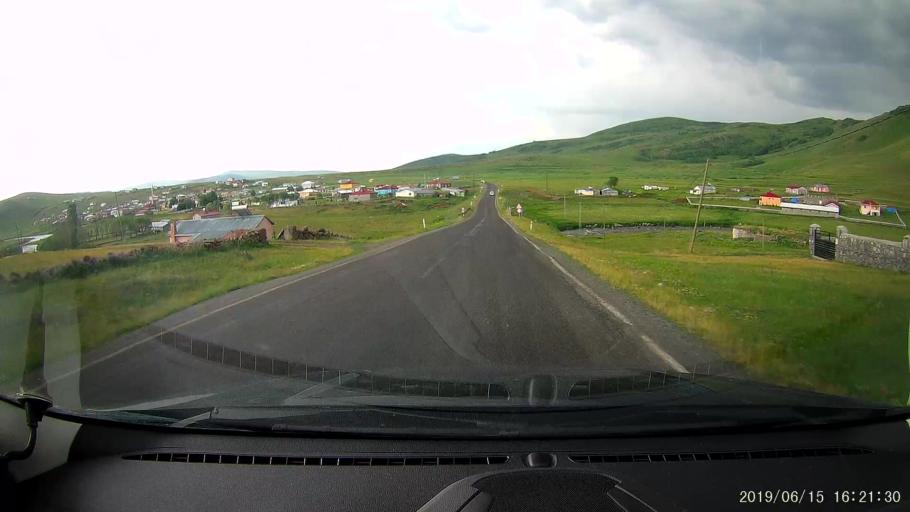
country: TR
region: Ardahan
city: Hanak
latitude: 41.1988
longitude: 42.8458
